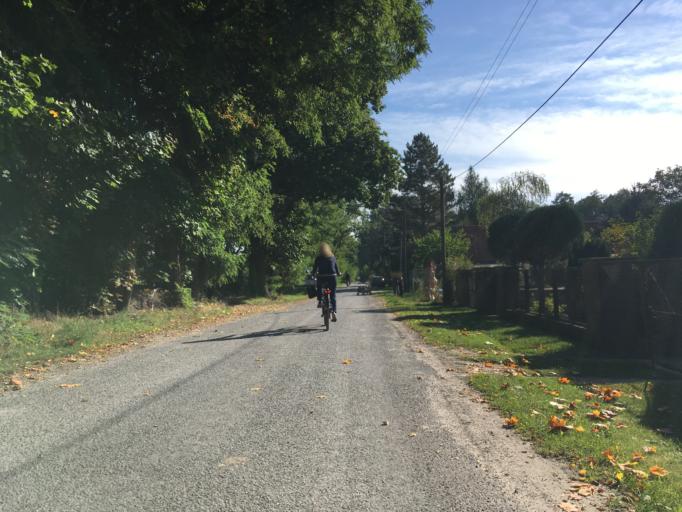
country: DE
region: Brandenburg
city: Altlandsberg
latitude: 52.5375
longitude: 13.7219
